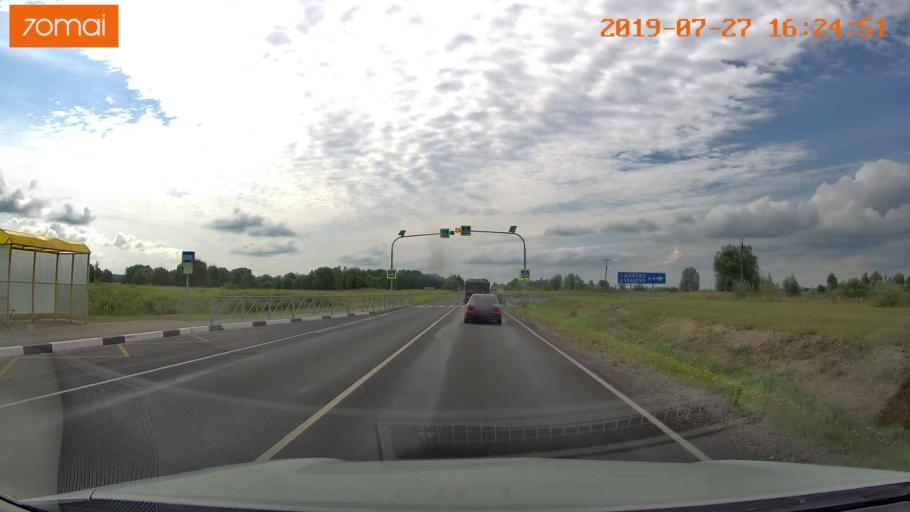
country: RU
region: Kaliningrad
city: Zheleznodorozhnyy
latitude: 54.6355
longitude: 21.4435
